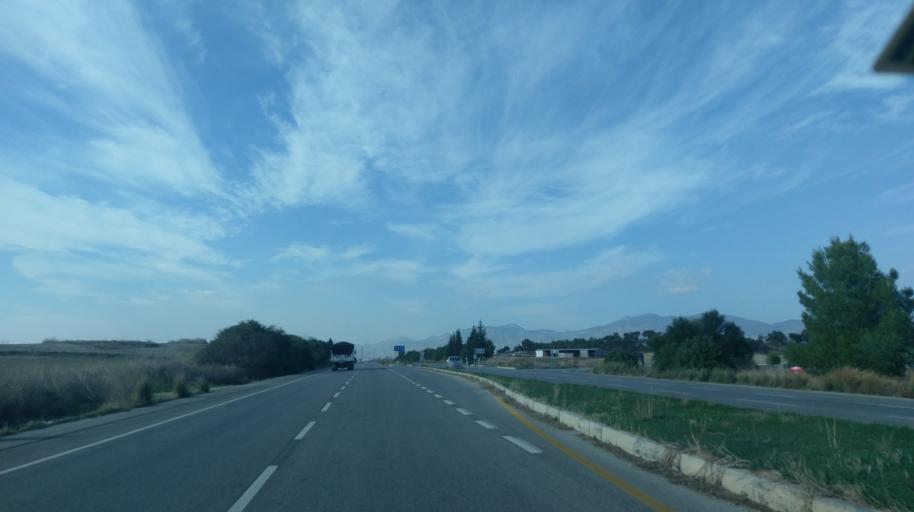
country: CY
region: Ammochostos
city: Lefkonoiko
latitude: 35.1946
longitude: 33.6192
